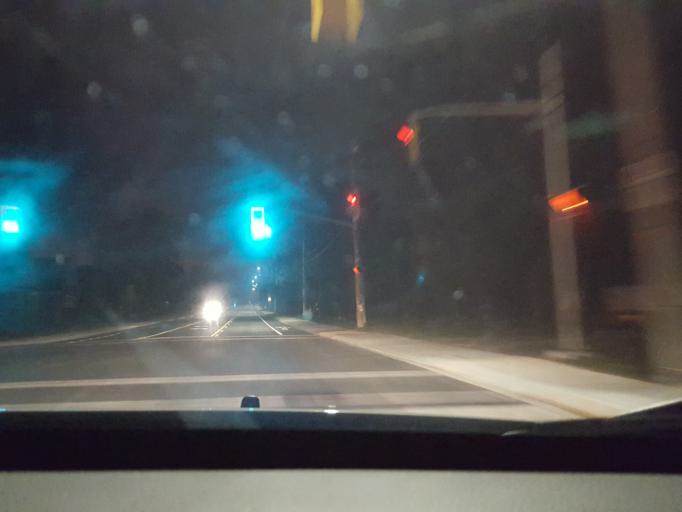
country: CA
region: Ontario
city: Hamilton
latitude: 43.2155
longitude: -79.8924
